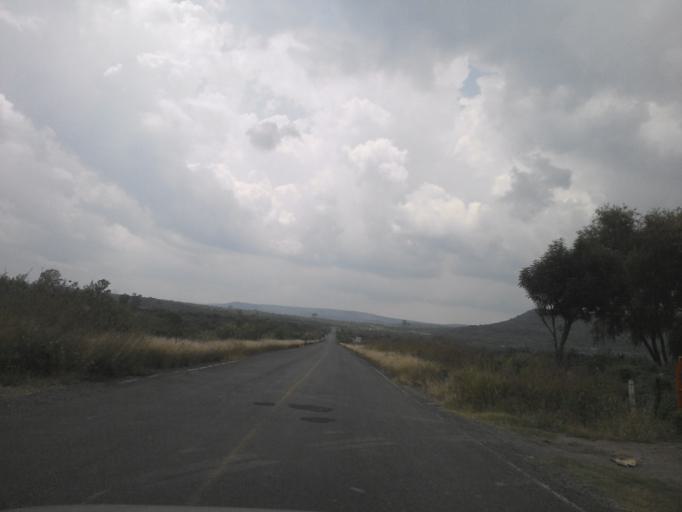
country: MX
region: Jalisco
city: San Diego de Alejandria
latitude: 20.8948
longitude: -101.9709
